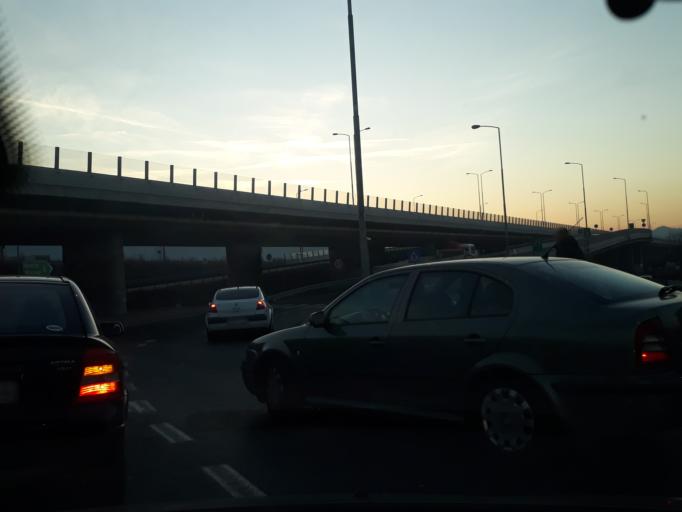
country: BA
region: Federation of Bosnia and Herzegovina
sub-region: Kanton Sarajevo
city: Sarajevo
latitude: 43.8518
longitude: 18.3261
